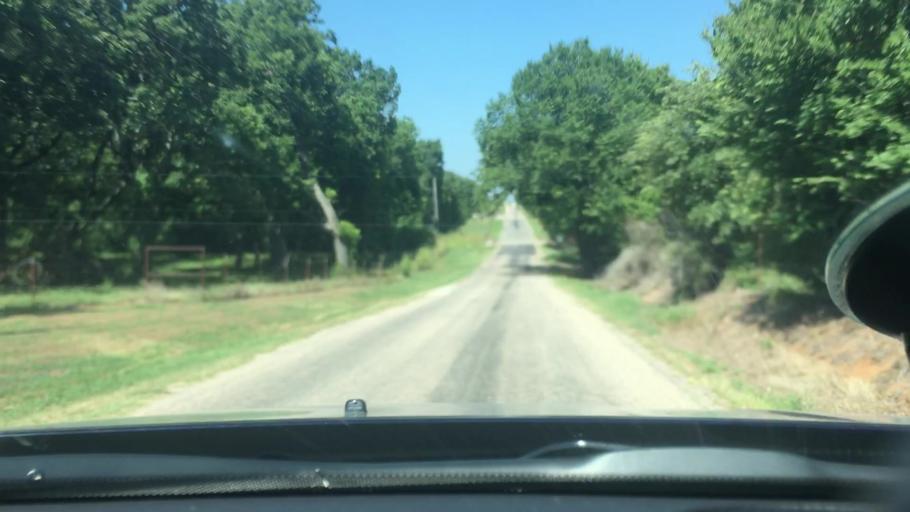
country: US
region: Oklahoma
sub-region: Johnston County
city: Tishomingo
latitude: 34.3177
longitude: -96.6499
